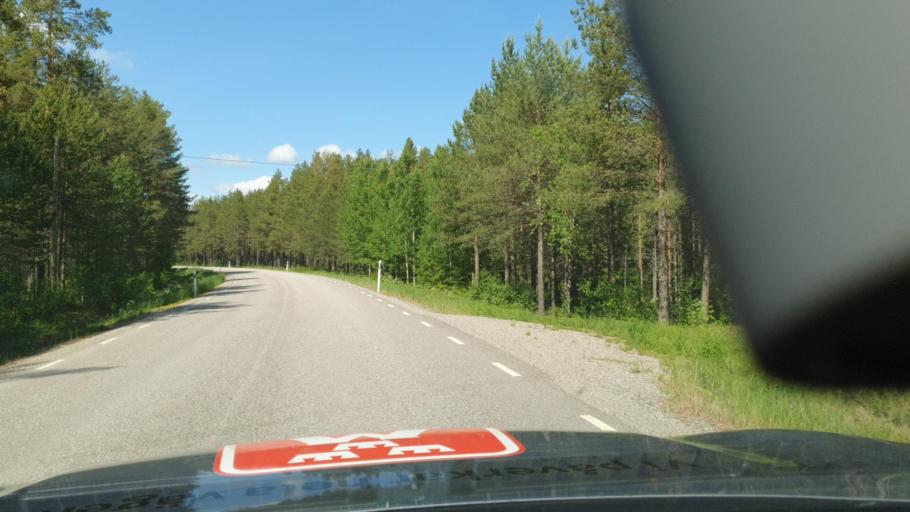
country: SE
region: Vaesternorrland
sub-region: Kramfors Kommun
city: Bollstabruk
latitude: 63.1143
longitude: 17.7574
